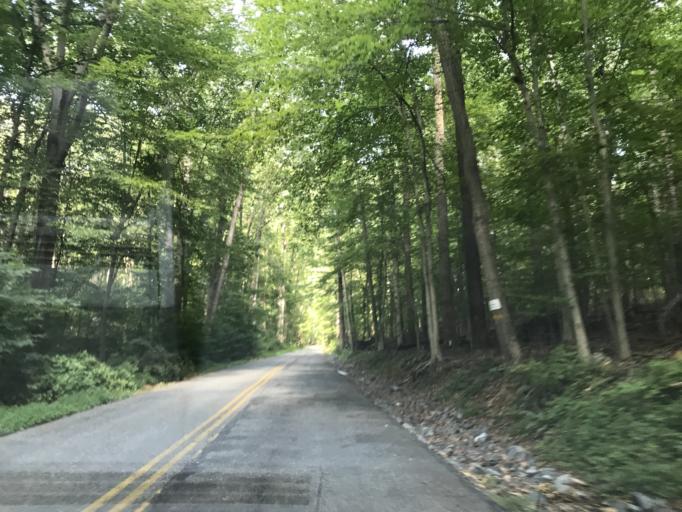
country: US
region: Maryland
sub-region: Harford County
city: South Bel Air
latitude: 39.6174
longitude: -76.2850
